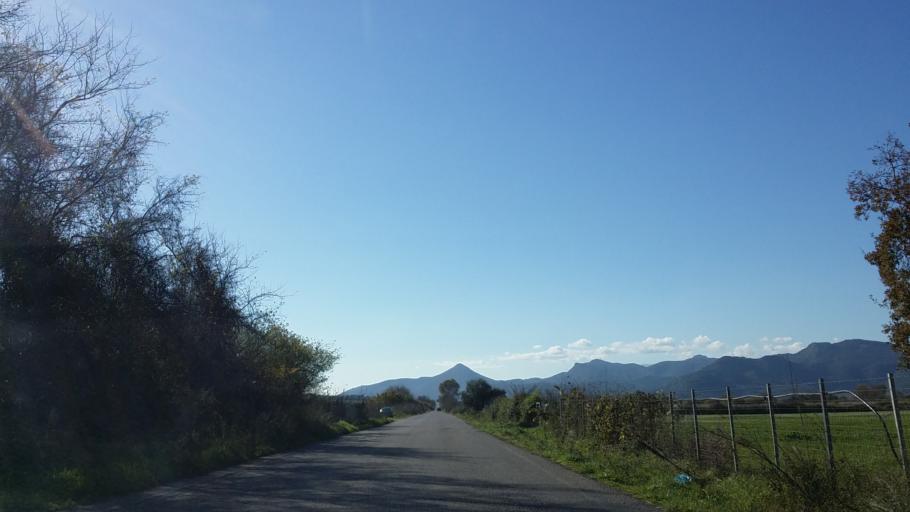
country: GR
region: West Greece
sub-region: Nomos Aitolias kai Akarnanias
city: Vonitsa
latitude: 38.8653
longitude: 20.8820
